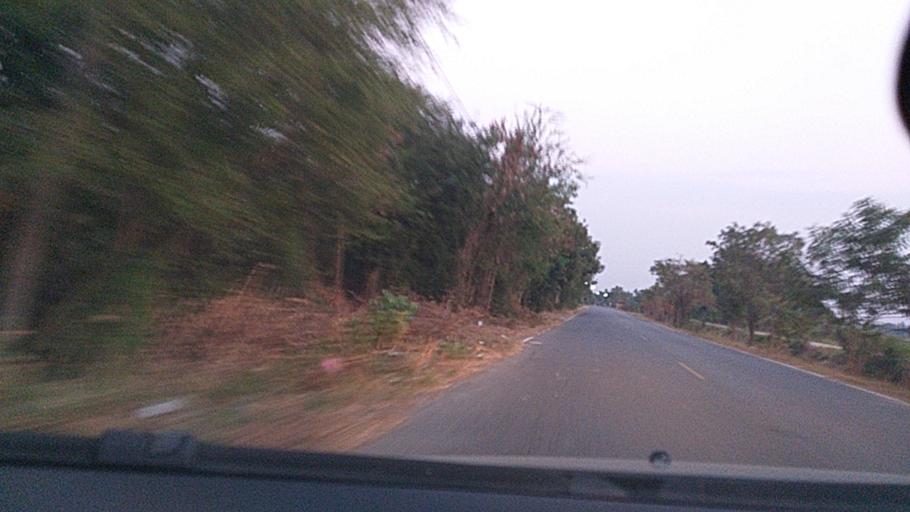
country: TH
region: Sing Buri
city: Sing Buri
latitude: 14.8296
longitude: 100.4035
